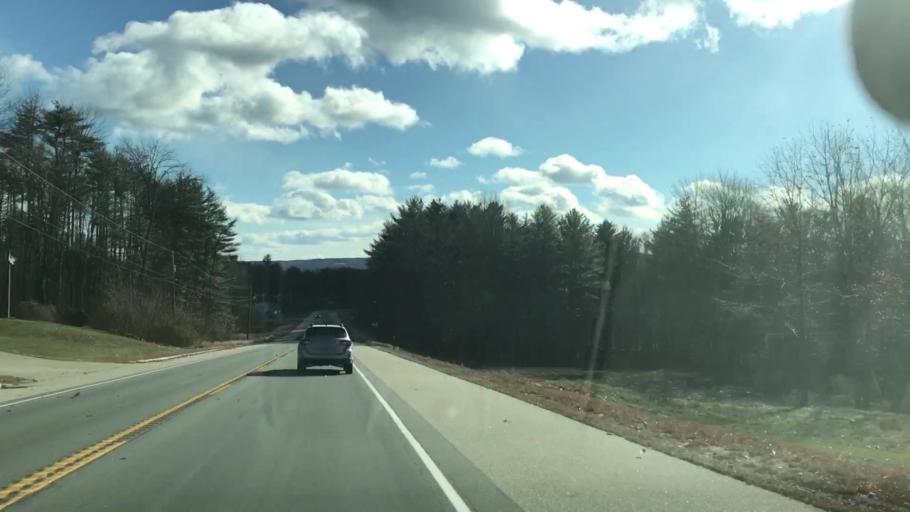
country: US
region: New Hampshire
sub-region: Strafford County
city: New Durham
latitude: 43.4604
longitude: -71.2200
